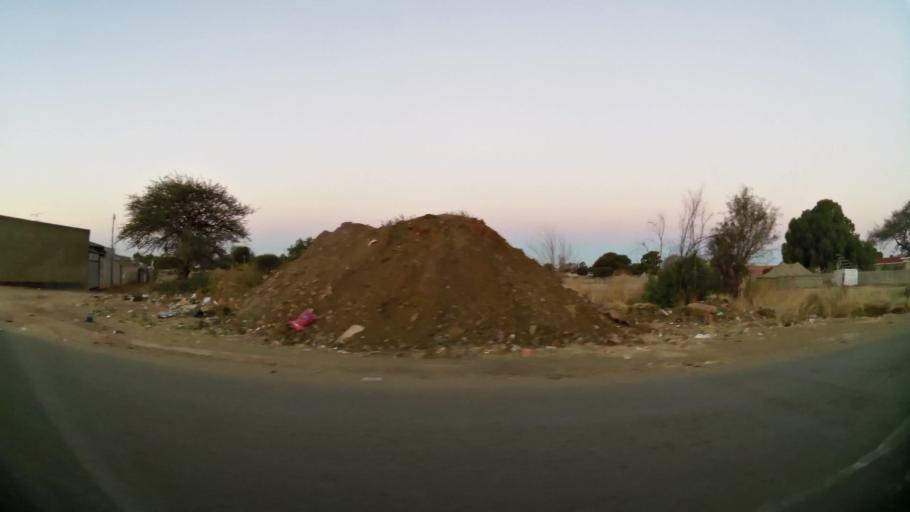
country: ZA
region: Northern Cape
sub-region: Frances Baard District Municipality
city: Kimberley
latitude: -28.7227
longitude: 24.7671
